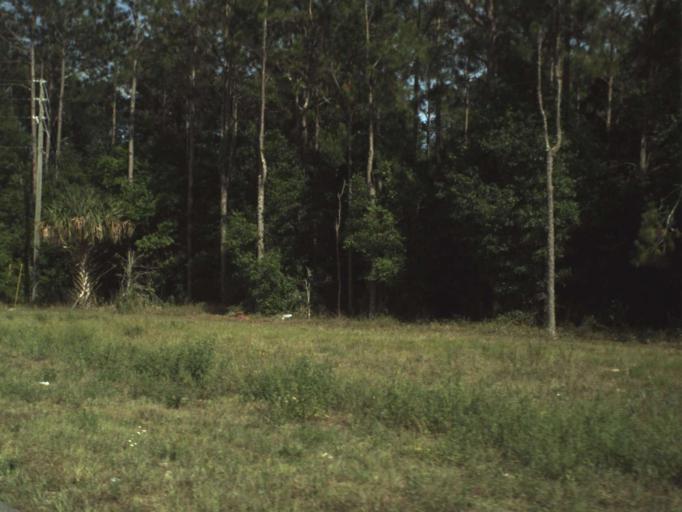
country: US
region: Florida
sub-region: Volusia County
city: West DeLand
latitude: 29.0273
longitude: -81.3438
